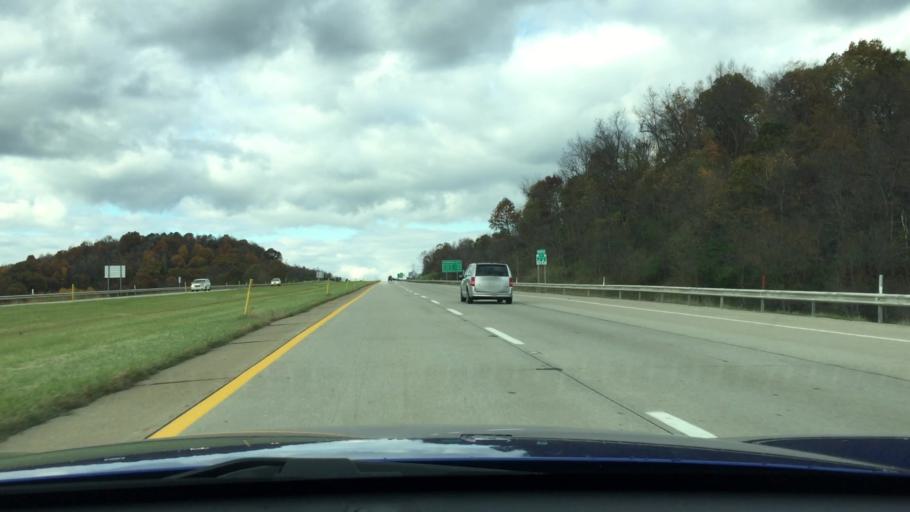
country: US
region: Pennsylvania
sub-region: Westmoreland County
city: New Stanton
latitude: 40.2415
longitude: -79.6066
